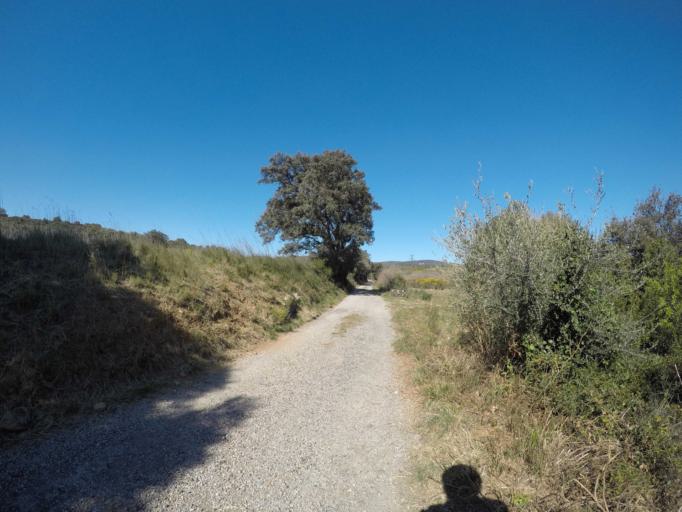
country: FR
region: Languedoc-Roussillon
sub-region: Departement des Pyrenees-Orientales
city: Millas
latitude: 42.7070
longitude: 2.6704
